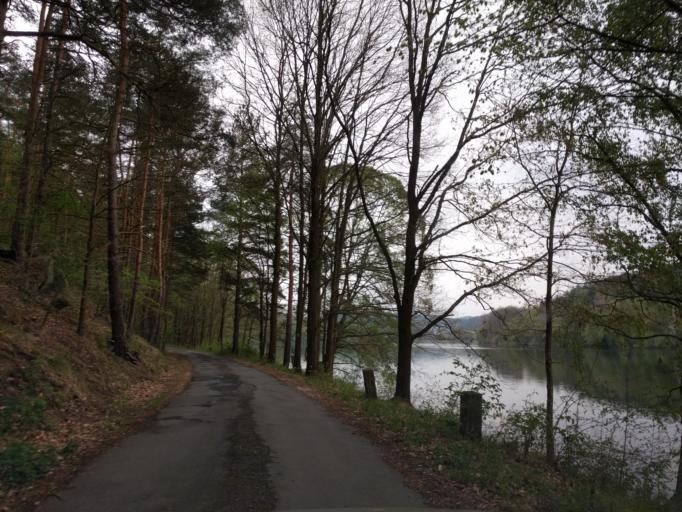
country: CZ
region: Central Bohemia
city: Krasna Hora nad Vltavou
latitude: 49.6730
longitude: 14.2637
